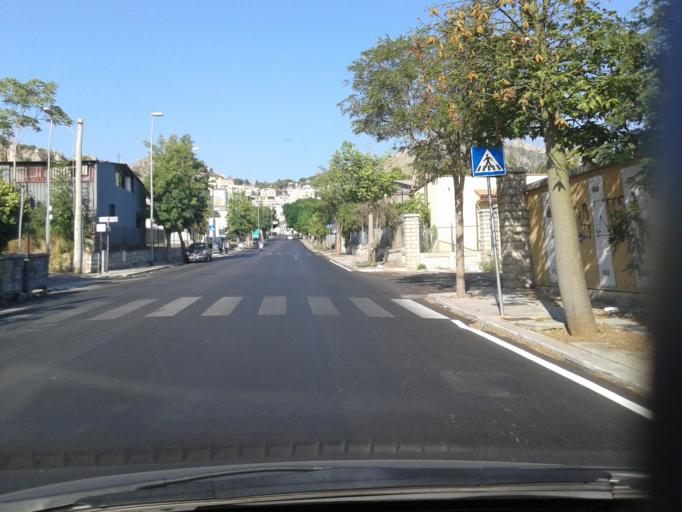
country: IT
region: Sicily
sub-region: Palermo
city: Palermo
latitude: 38.1095
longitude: 13.3121
